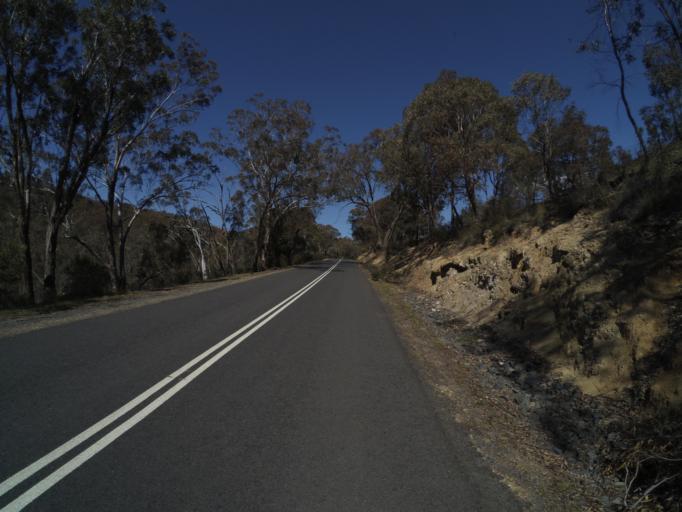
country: AU
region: Australian Capital Territory
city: Macquarie
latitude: -35.1701
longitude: 148.8892
